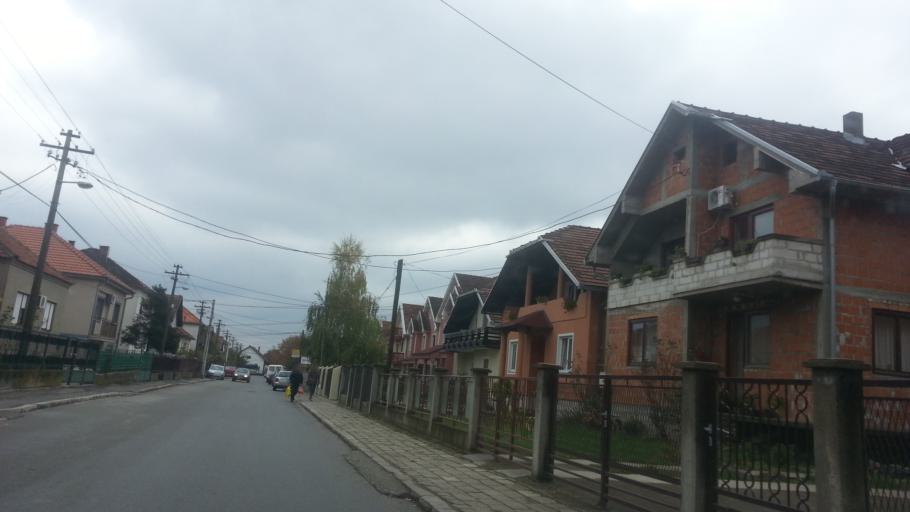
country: RS
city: Novi Banovci
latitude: 44.9079
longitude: 20.2854
